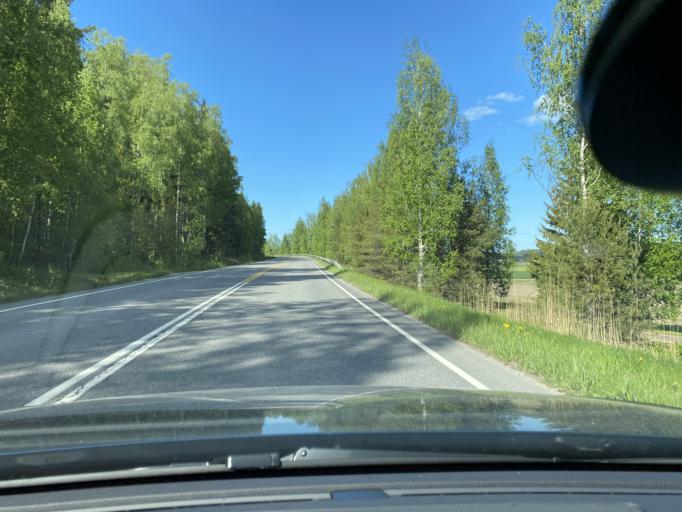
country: FI
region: Varsinais-Suomi
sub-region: Turku
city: Sauvo
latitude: 60.3574
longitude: 22.6698
